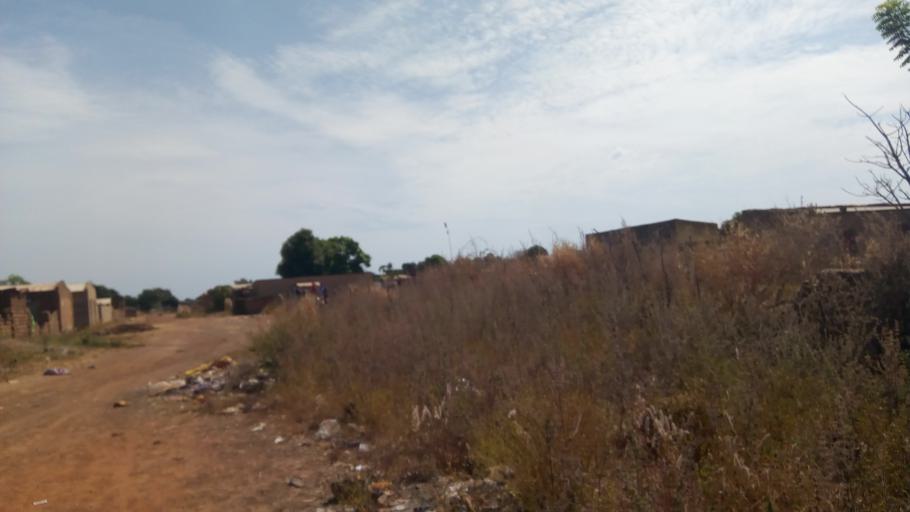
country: ML
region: Koulikoro
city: Kangaba
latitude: 11.9883
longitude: -7.9025
